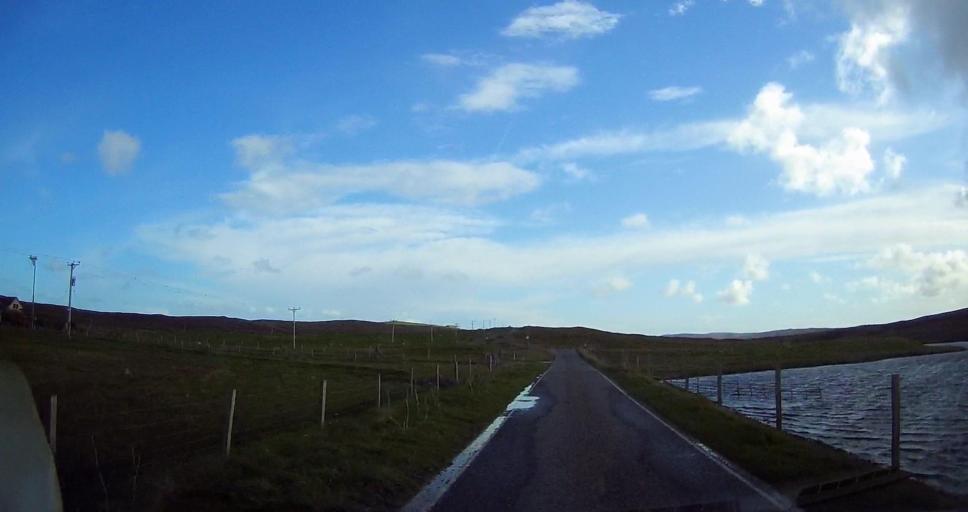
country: GB
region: Scotland
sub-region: Shetland Islands
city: Shetland
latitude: 60.3674
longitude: -1.1411
